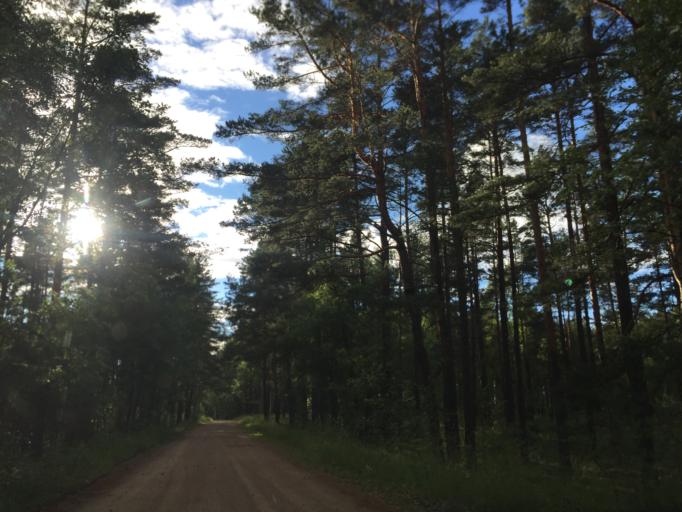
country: LV
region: Carnikava
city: Carnikava
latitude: 57.1711
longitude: 24.3552
